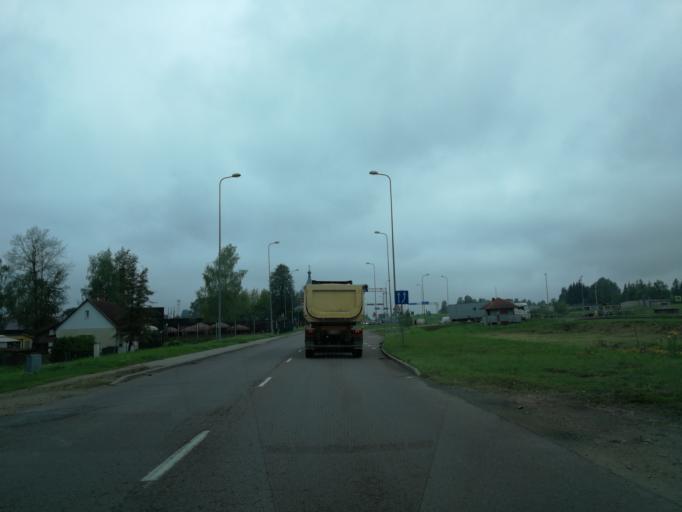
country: LV
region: Jekabpils Rajons
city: Jekabpils
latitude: 56.5034
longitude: 25.8917
